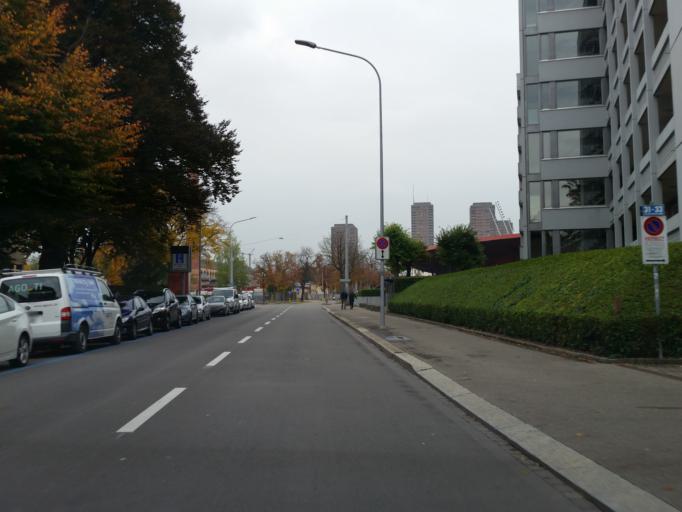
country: CH
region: Zurich
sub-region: Bezirk Zuerich
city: Zuerich (Kreis 4) / Hard
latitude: 47.3849
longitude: 8.5017
